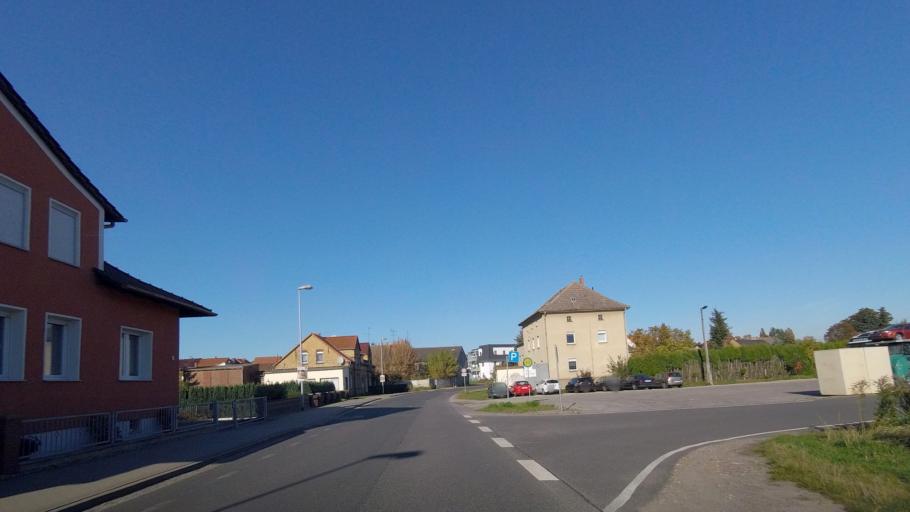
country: DE
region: Saxony-Anhalt
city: Zahna
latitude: 51.9151
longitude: 12.7826
